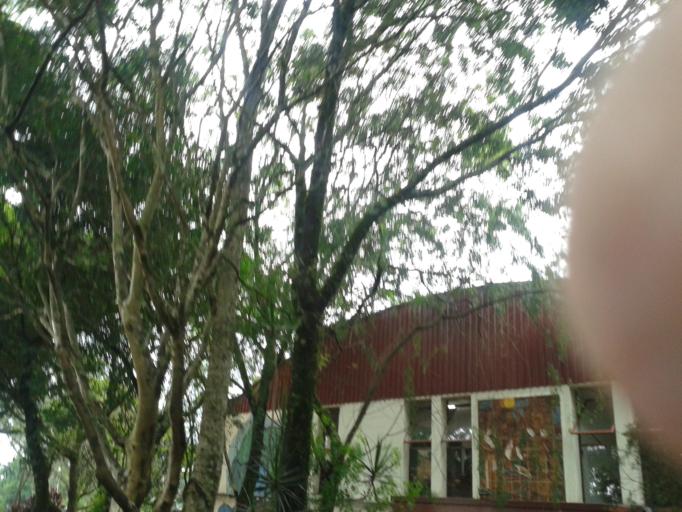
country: AR
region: Misiones
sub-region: Departamento de Obera
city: Obera
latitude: -27.4858
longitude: -55.1099
